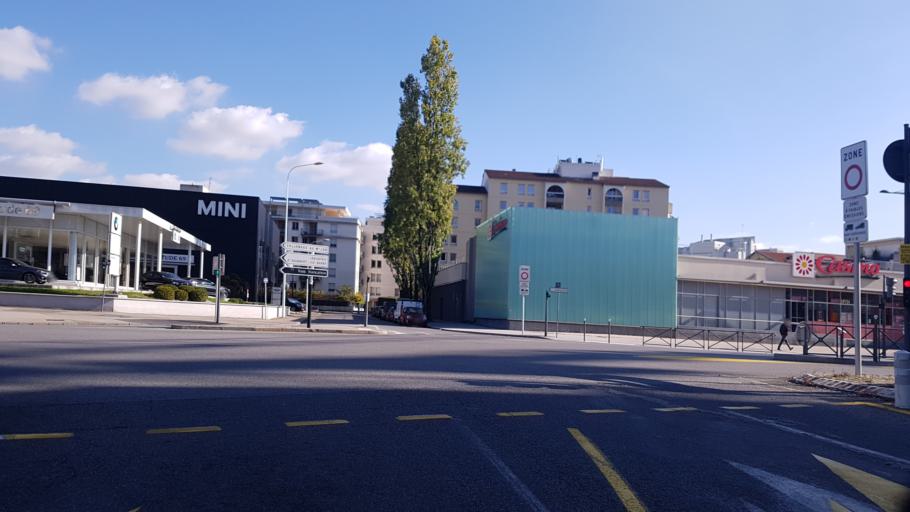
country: FR
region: Rhone-Alpes
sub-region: Departement du Rhone
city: Caluire-et-Cuire
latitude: 45.7848
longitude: 4.8082
